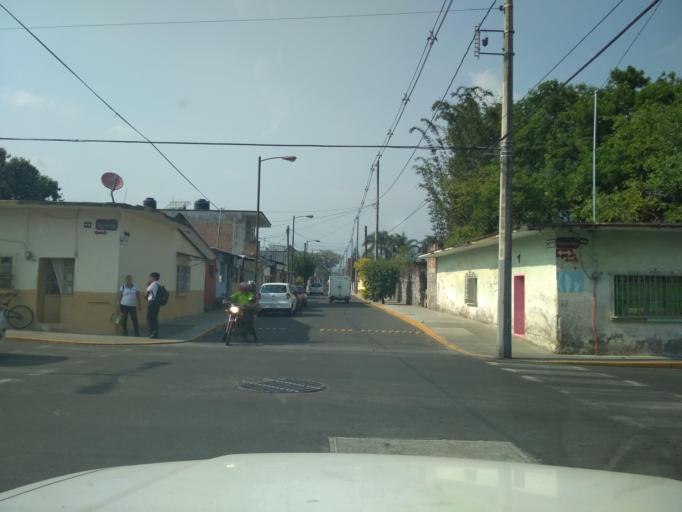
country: MX
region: Veracruz
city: Orizaba
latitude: 18.8408
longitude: -97.0892
